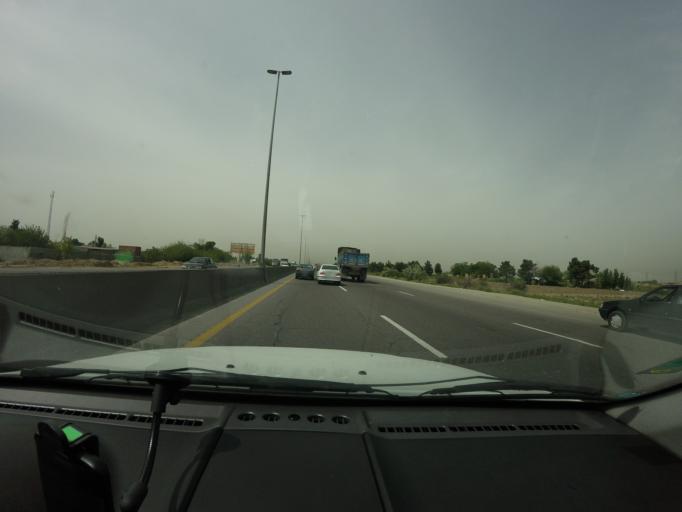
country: IR
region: Tehran
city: Eslamshahr
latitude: 35.6083
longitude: 51.2011
